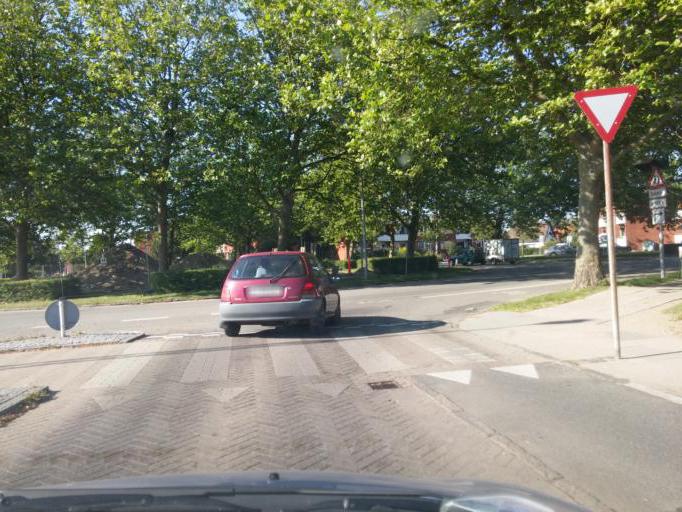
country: DK
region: South Denmark
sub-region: Odense Kommune
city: Odense
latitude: 55.3865
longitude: 10.4166
